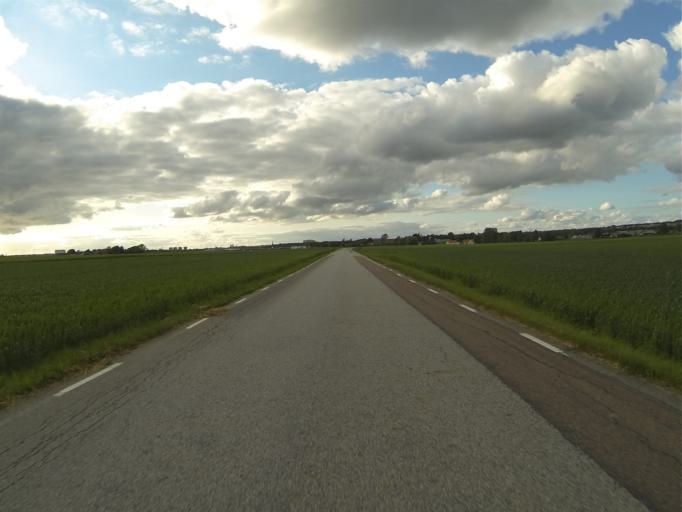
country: SE
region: Skane
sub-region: Staffanstorps Kommun
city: Staffanstorp
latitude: 55.6793
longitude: 13.2269
